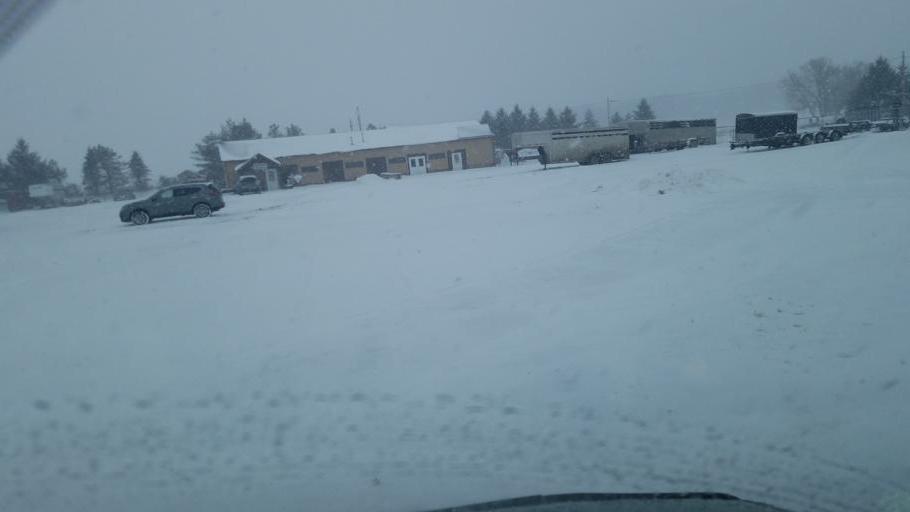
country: US
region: Ohio
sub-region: Geauga County
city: Middlefield
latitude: 41.4800
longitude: -81.0750
